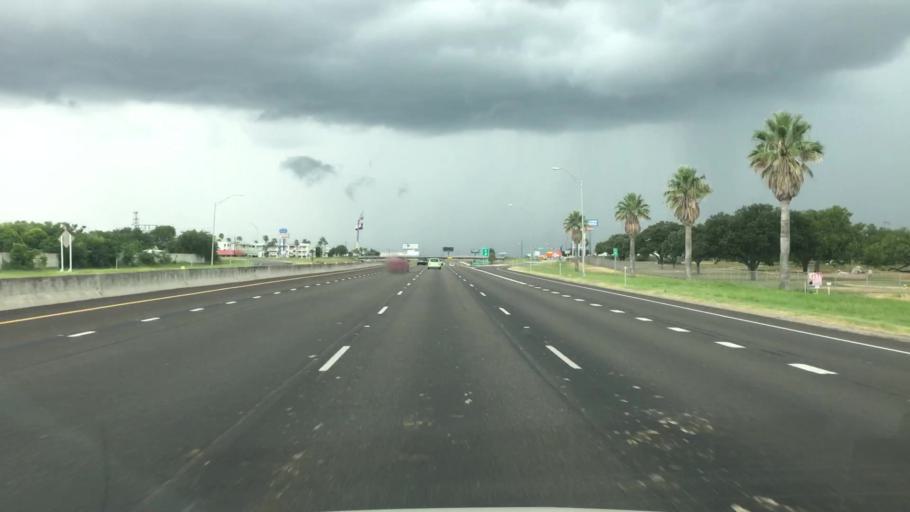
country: US
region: Texas
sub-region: Nueces County
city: Corpus Christi
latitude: 27.8048
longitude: -97.4800
